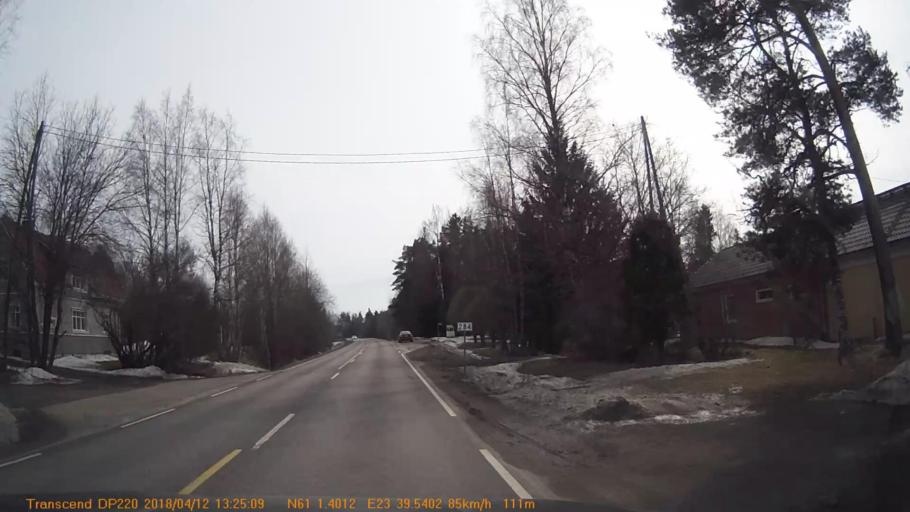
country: FI
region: Pirkanmaa
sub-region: Etelae-Pirkanmaa
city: Kylmaekoski
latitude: 61.0231
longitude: 23.6592
